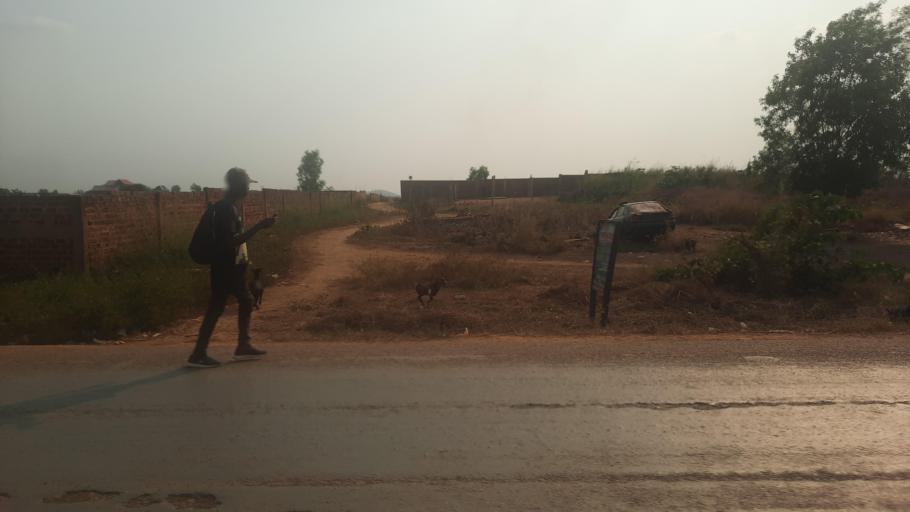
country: AO
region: Zaire
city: Mbanza Congo
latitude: -5.8195
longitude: 14.0709
